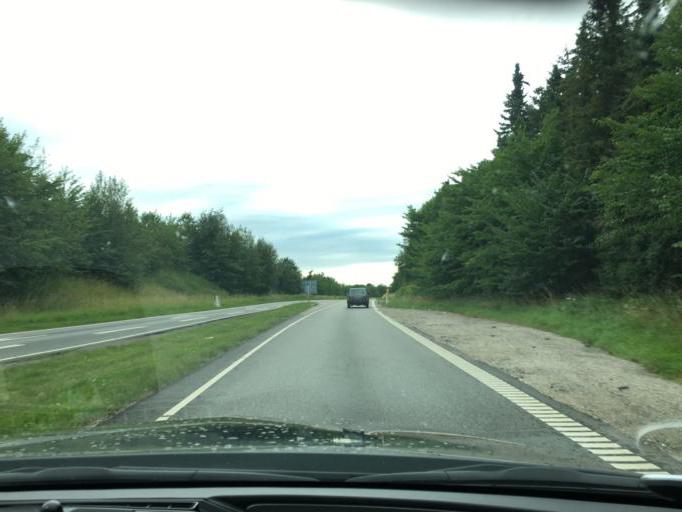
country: DK
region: Capital Region
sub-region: Rudersdal Kommune
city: Birkerod
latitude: 55.8832
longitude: 12.4542
